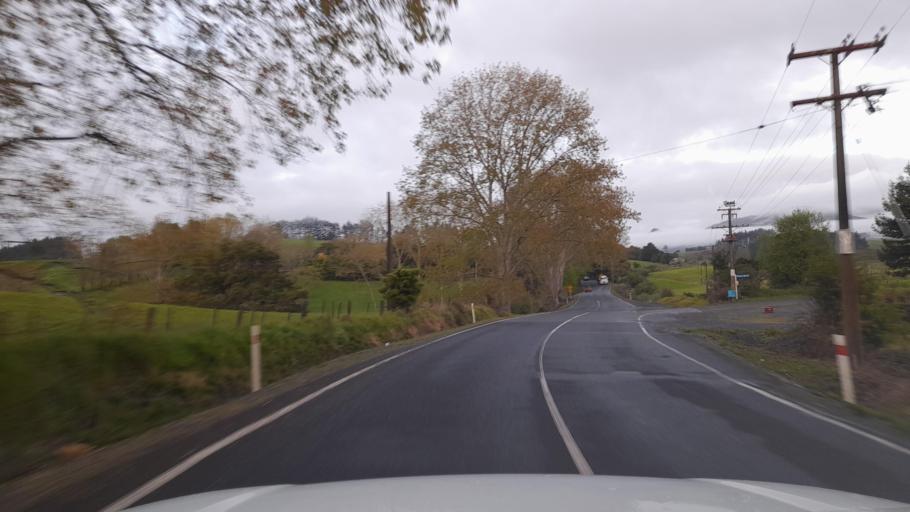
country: NZ
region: Northland
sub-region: Whangarei
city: Maungatapere
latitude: -35.7069
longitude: 174.0224
